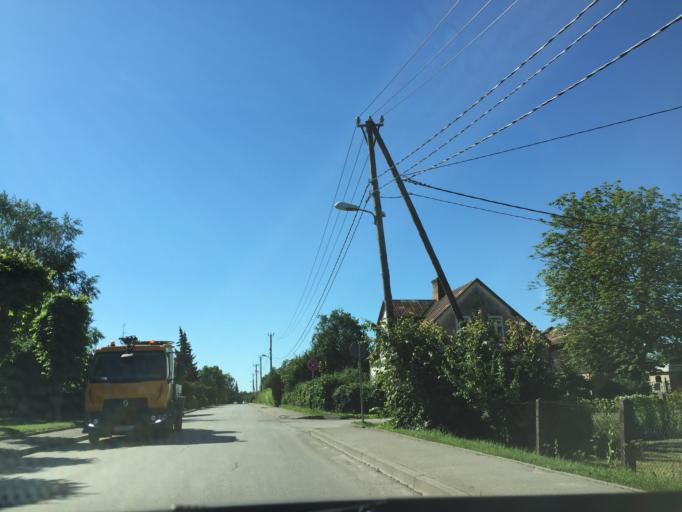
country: LV
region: Bauskas Rajons
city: Bauska
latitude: 56.4054
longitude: 24.1902
